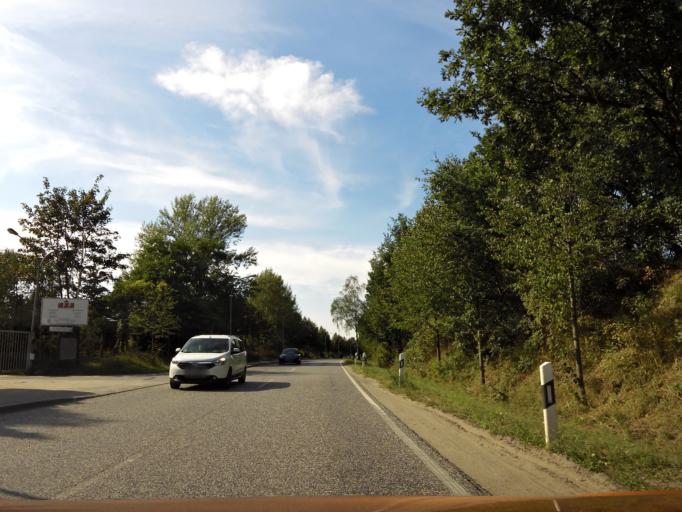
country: DE
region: Brandenburg
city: Teltow
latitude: 52.3789
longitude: 13.2535
